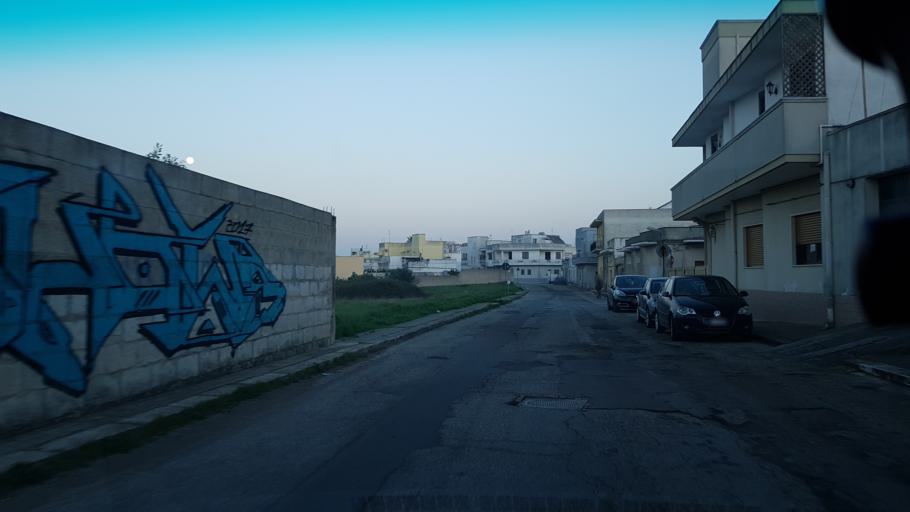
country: IT
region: Apulia
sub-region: Provincia di Brindisi
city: Mesagne
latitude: 40.5636
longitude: 17.7961
